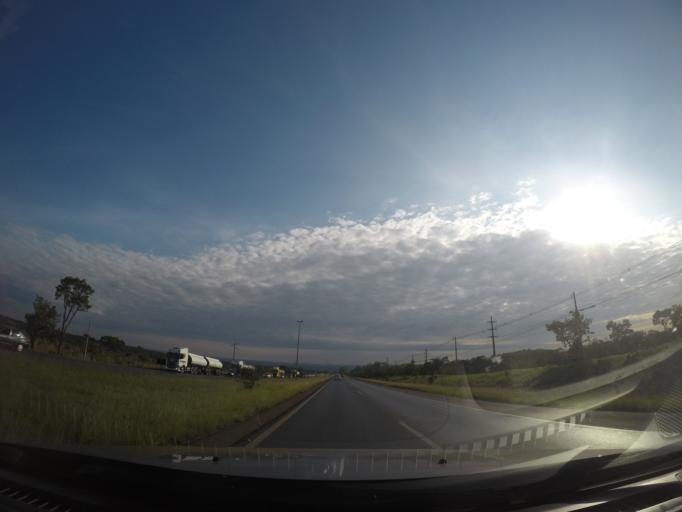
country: BR
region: Goias
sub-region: Planaltina
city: Planaltina
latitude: -15.6311
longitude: -47.7347
